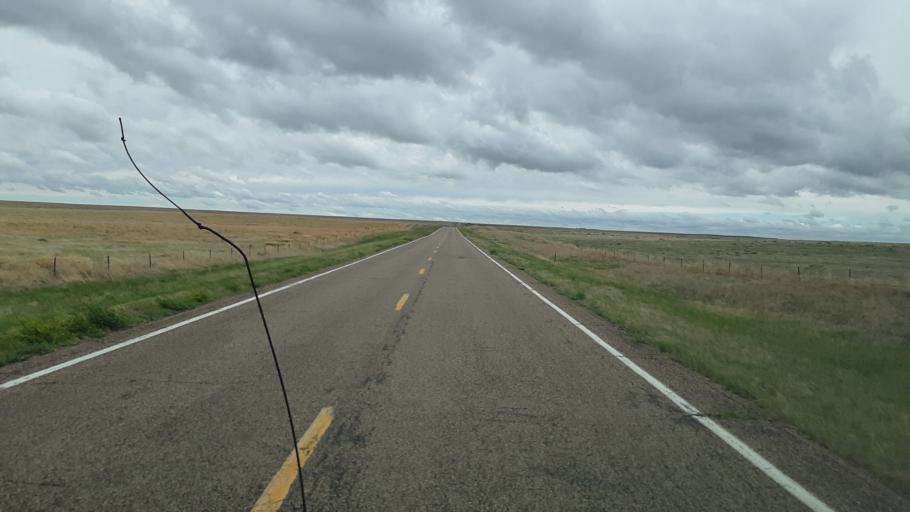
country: US
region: Colorado
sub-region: Lincoln County
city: Hugo
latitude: 38.8509
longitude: -103.6027
